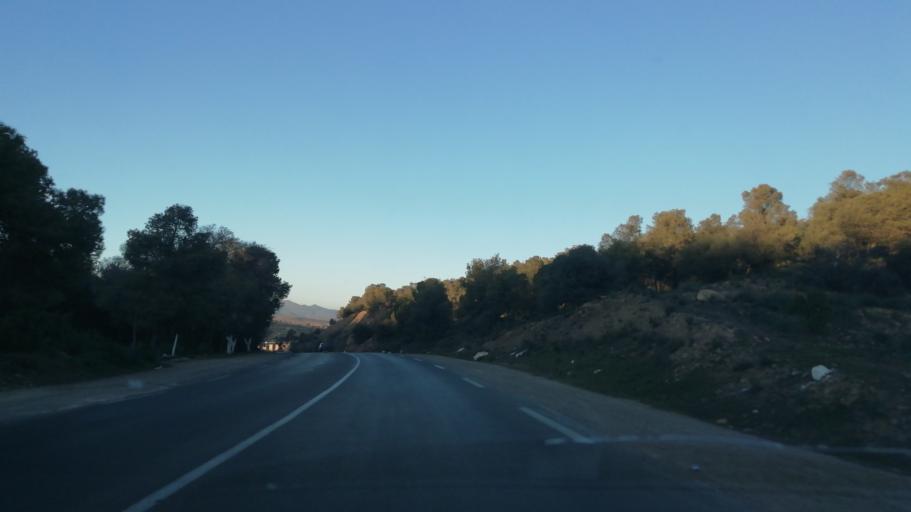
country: DZ
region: Tlemcen
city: Nedroma
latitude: 34.8751
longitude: -1.6682
